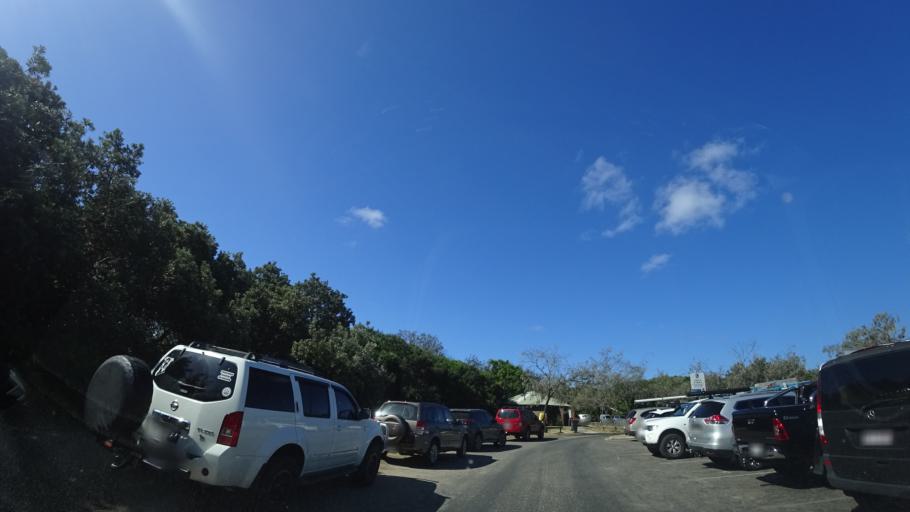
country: AU
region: Queensland
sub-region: Sunshine Coast
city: Mooloolaba
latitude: -26.6393
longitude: 153.1002
